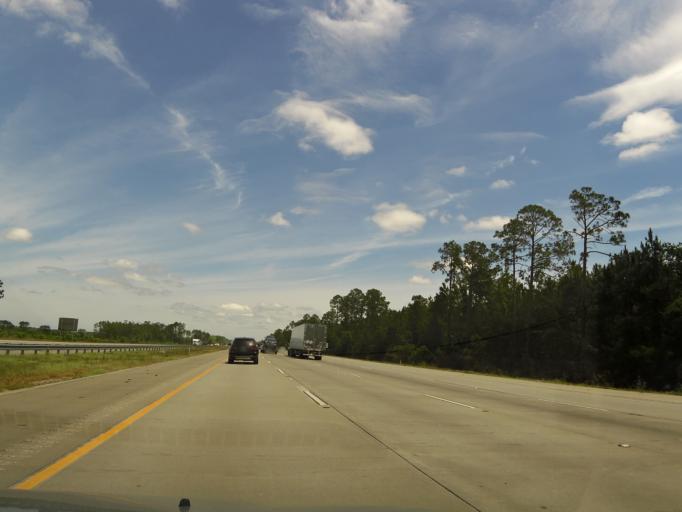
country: US
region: Georgia
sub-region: Glynn County
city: Country Club Estates
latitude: 31.2600
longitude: -81.4953
